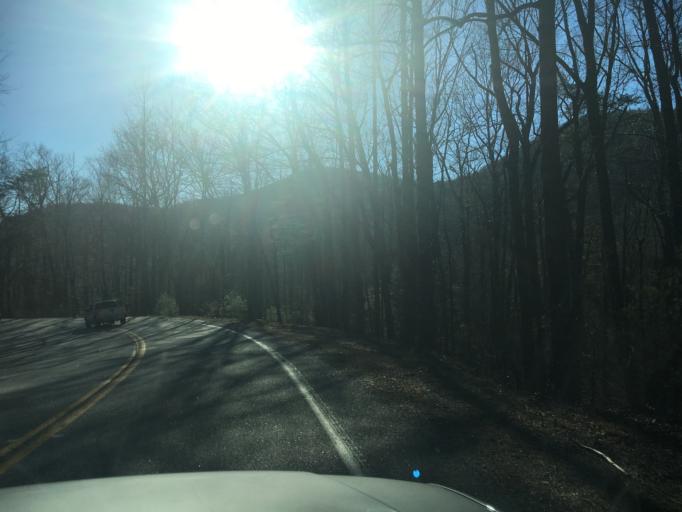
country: US
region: Georgia
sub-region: Union County
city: Blairsville
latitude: 34.7127
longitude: -83.9115
